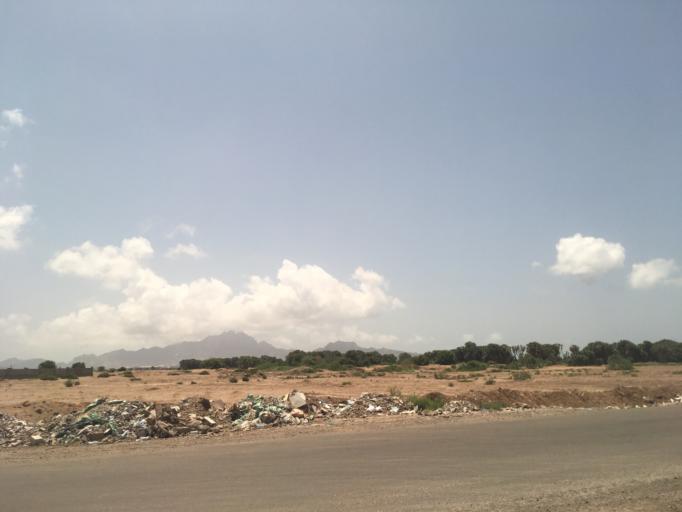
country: YE
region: Aden
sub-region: Al Mansura
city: Al Mansurah
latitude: 12.8476
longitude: 44.9713
